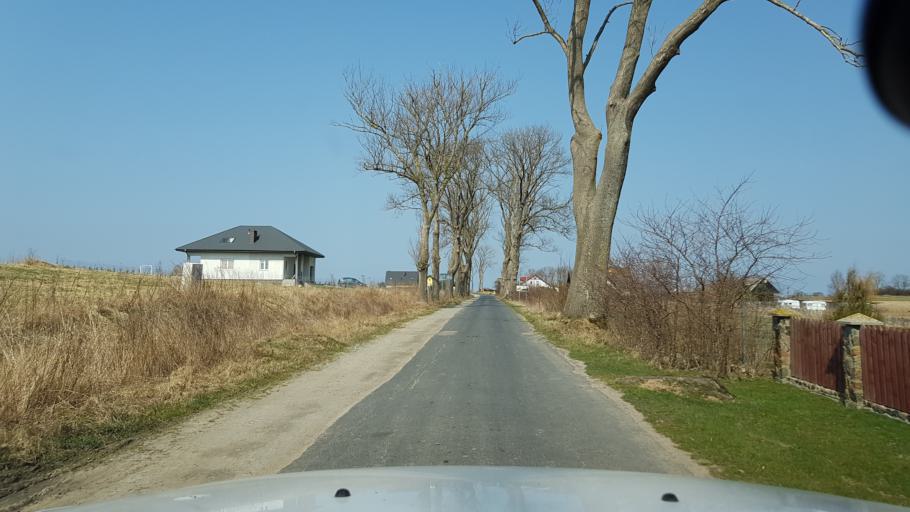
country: PL
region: West Pomeranian Voivodeship
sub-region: Powiat slawienski
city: Darlowo
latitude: 54.4502
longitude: 16.4342
